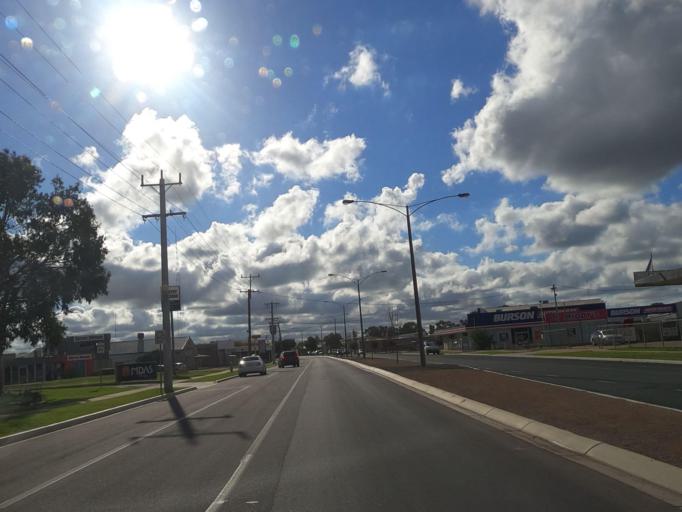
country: AU
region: Victoria
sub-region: Swan Hill
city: Swan Hill
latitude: -35.3328
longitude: 143.5556
